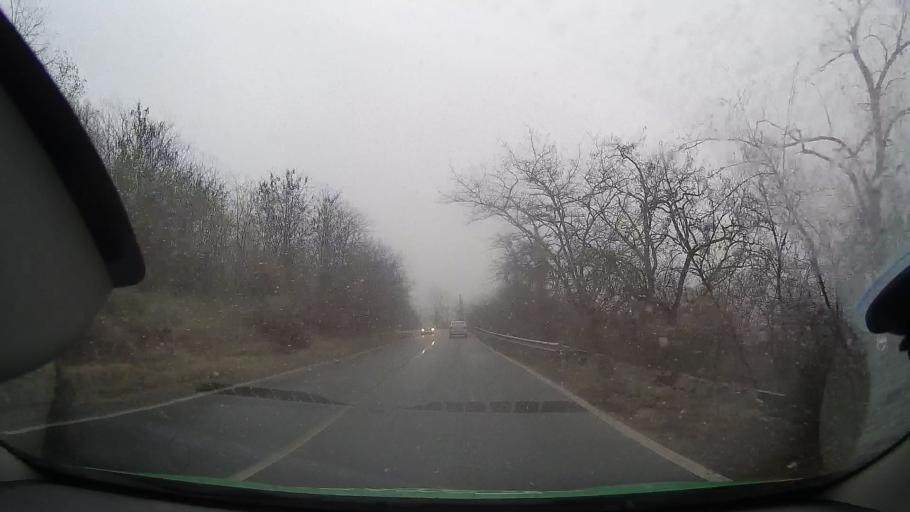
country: RO
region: Sibiu
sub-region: Municipiul Medias
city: Medias
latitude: 46.1818
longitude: 24.3333
